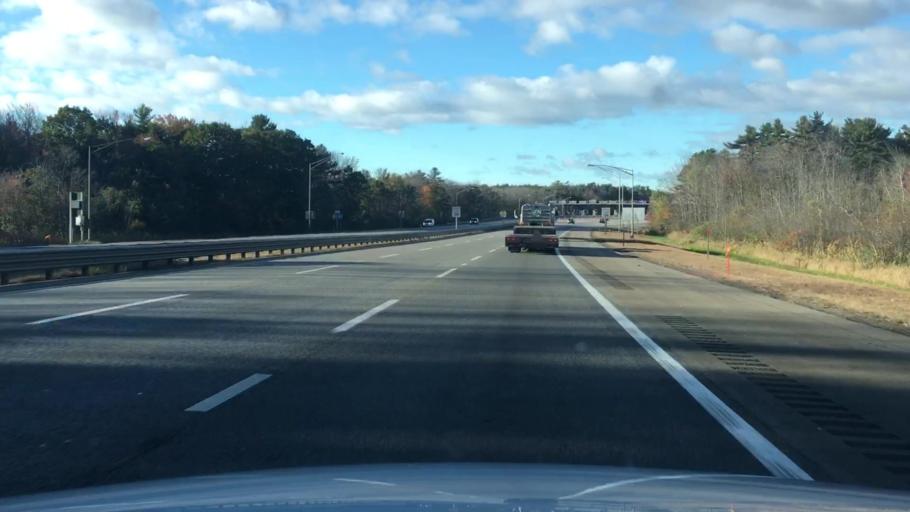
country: US
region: Maine
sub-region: York County
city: York Harbor
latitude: 43.1631
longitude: -70.6560
